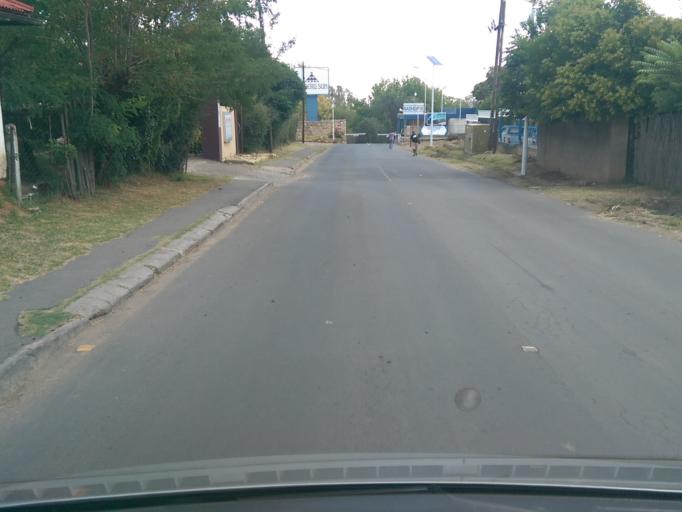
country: LS
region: Maseru
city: Maseru
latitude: -29.3155
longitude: 27.4739
